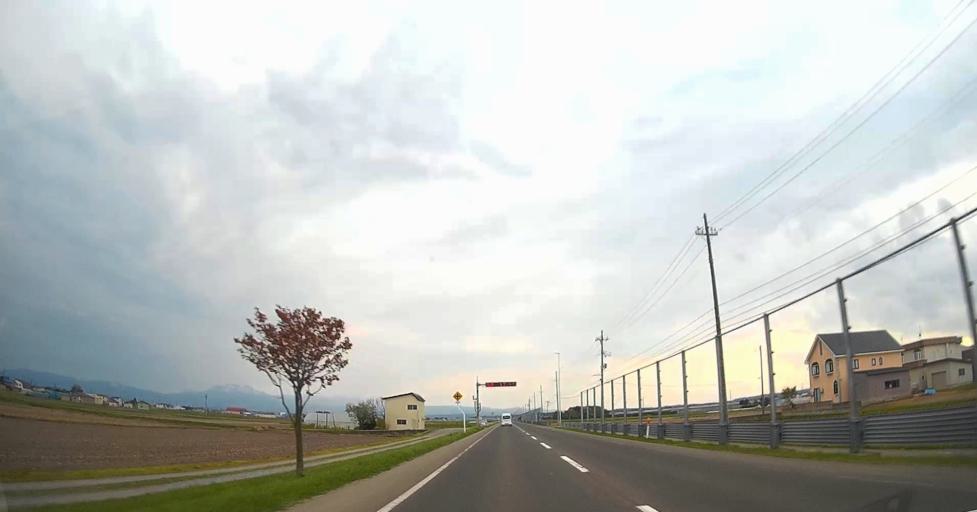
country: JP
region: Aomori
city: Aomori Shi
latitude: 40.8882
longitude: 140.6694
